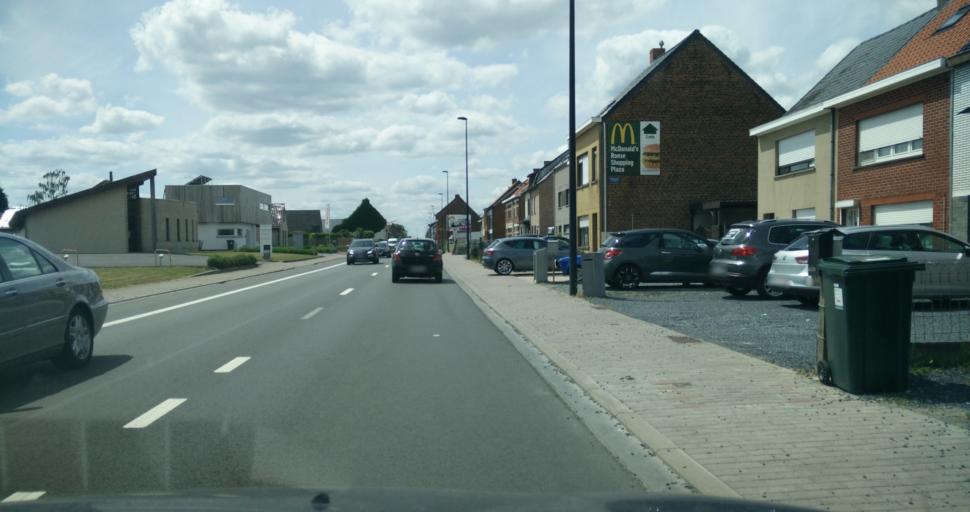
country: BE
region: Flanders
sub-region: Provincie Oost-Vlaanderen
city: Ronse
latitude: 50.7528
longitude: 3.6305
